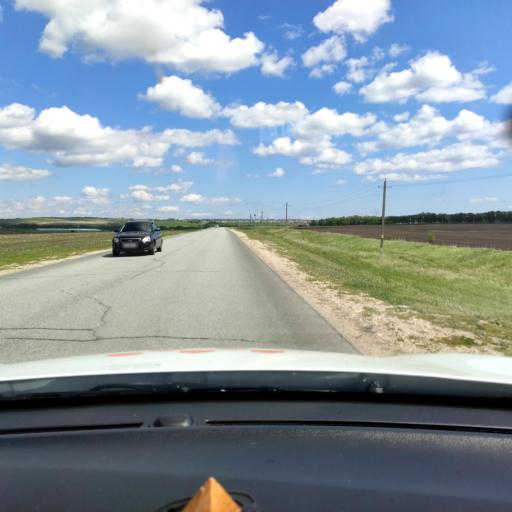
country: RU
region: Tatarstan
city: Kuybyshevskiy Zaton
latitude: 55.1655
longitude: 49.2053
